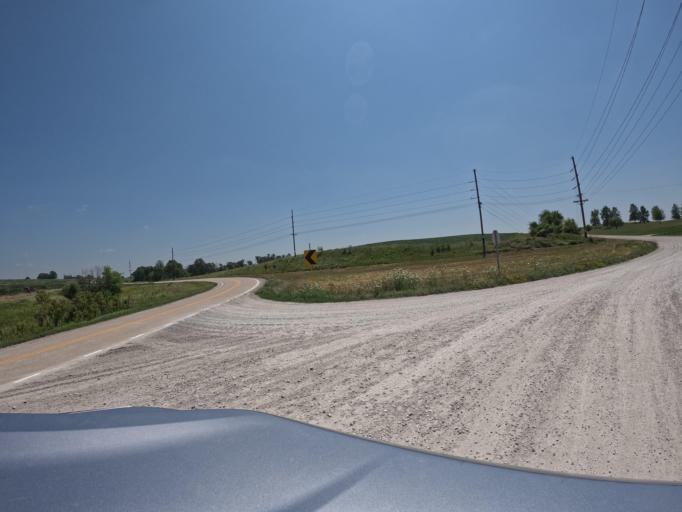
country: US
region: Iowa
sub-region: Keokuk County
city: Sigourney
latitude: 41.2763
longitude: -92.1805
